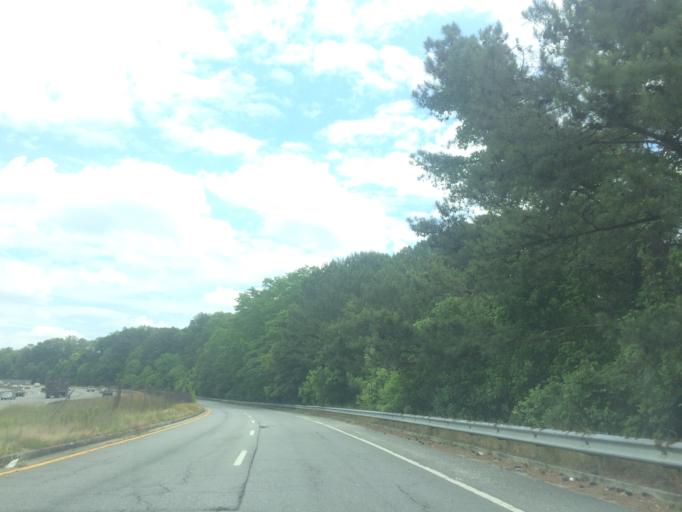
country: US
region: Georgia
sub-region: DeKalb County
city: North Druid Hills
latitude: 33.8406
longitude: -84.3099
